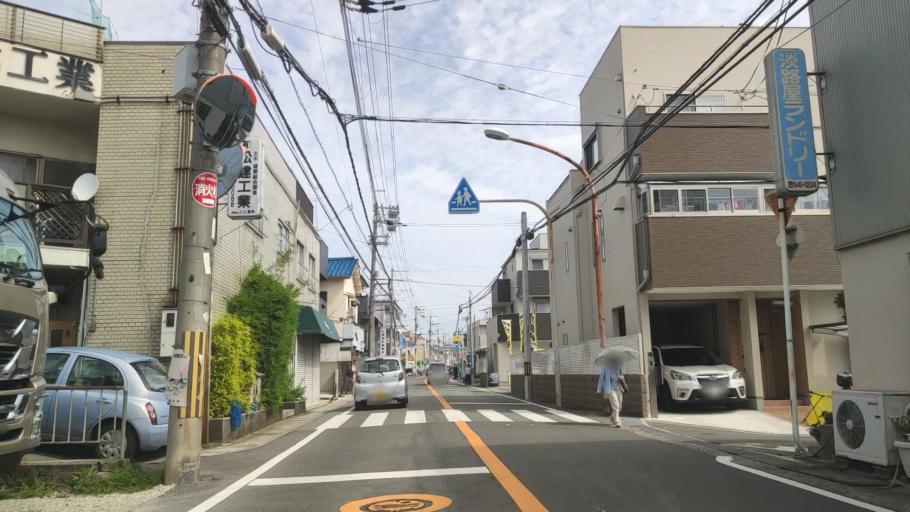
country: JP
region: Osaka
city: Mino
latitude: 34.8104
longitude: 135.4666
